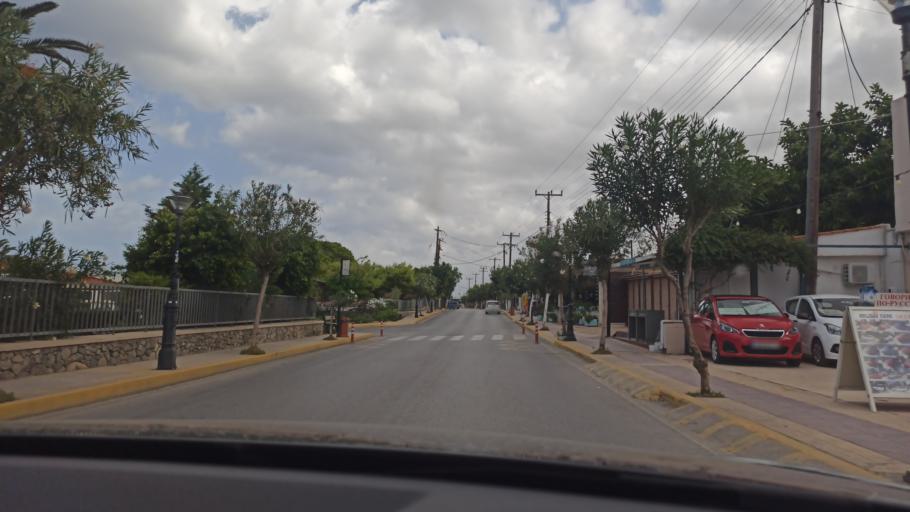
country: GR
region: Crete
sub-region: Nomos Irakleiou
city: Gazi
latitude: 35.3358
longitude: 25.0800
